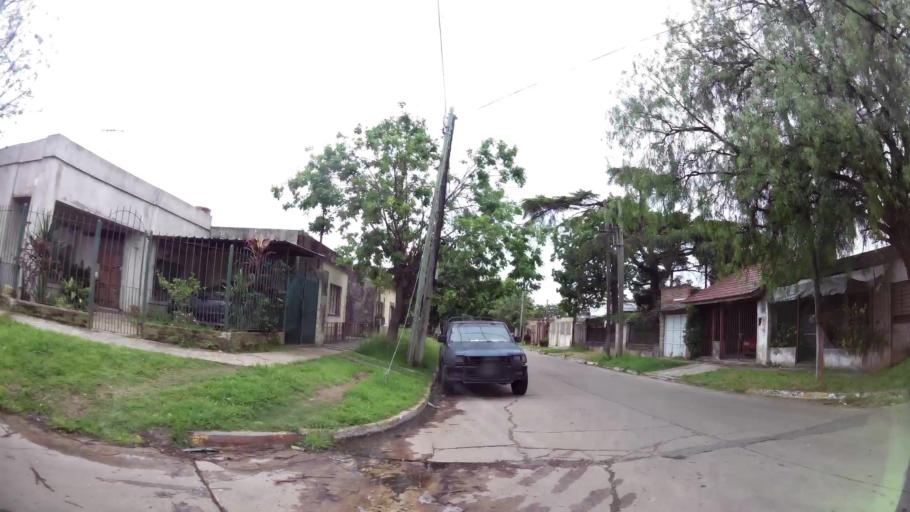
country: AR
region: Buenos Aires
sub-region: Partido de Quilmes
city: Quilmes
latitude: -34.7579
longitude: -58.2329
